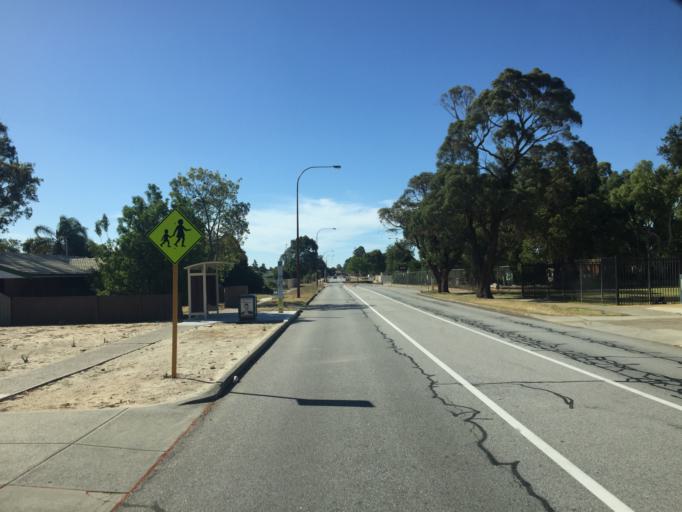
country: AU
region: Western Australia
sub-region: Gosnells
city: Maddington
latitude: -32.0563
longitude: 116.0035
